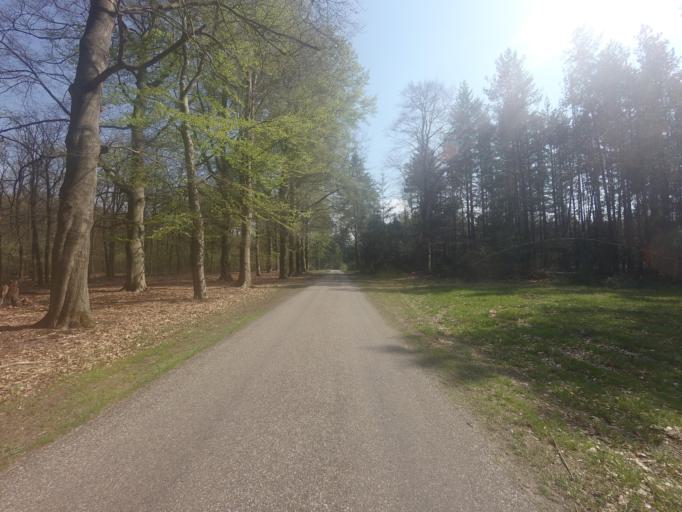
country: NL
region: North Holland
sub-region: Gemeente Hilversum
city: Hilversum
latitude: 52.1938
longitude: 5.2175
